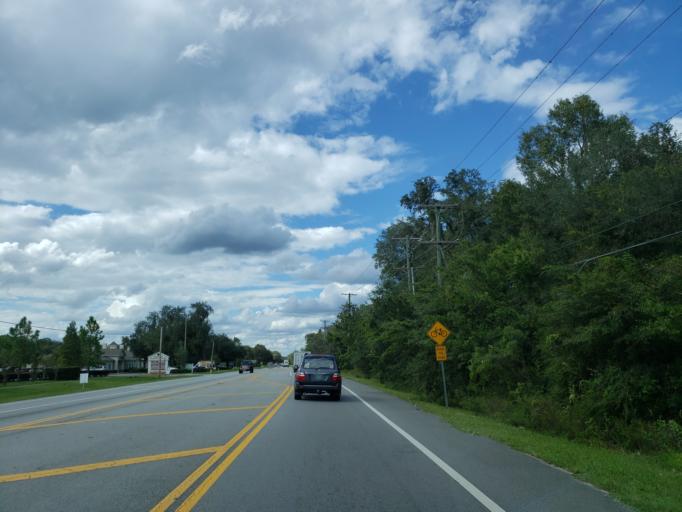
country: US
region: Florida
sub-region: Hillsborough County
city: Fish Hawk
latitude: 27.8630
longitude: -82.2019
